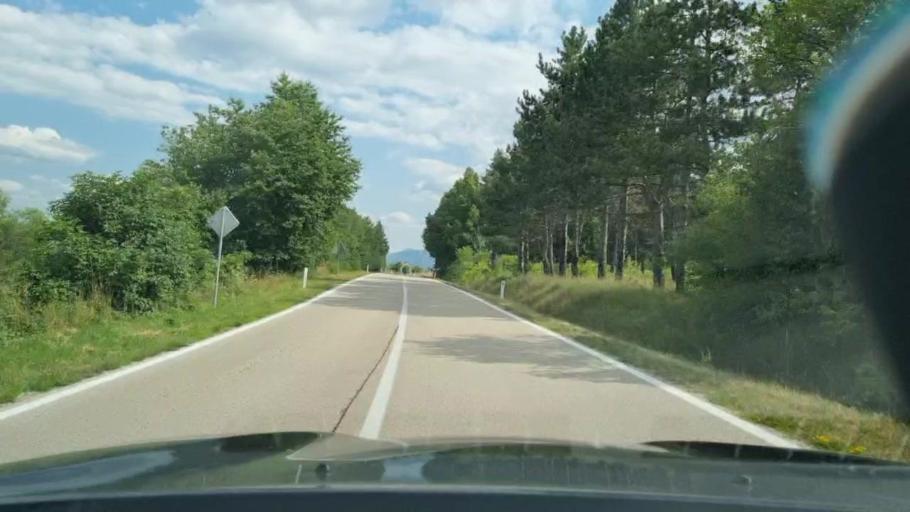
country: BA
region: Federation of Bosnia and Herzegovina
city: Bosansko Grahovo
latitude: 44.0852
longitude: 16.5686
